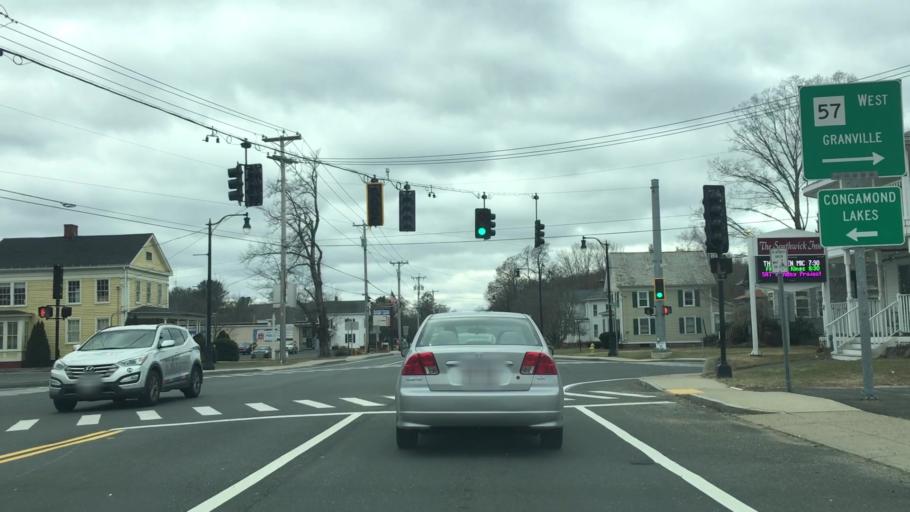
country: US
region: Massachusetts
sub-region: Hampden County
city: Southwick
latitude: 42.0550
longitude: -72.7700
